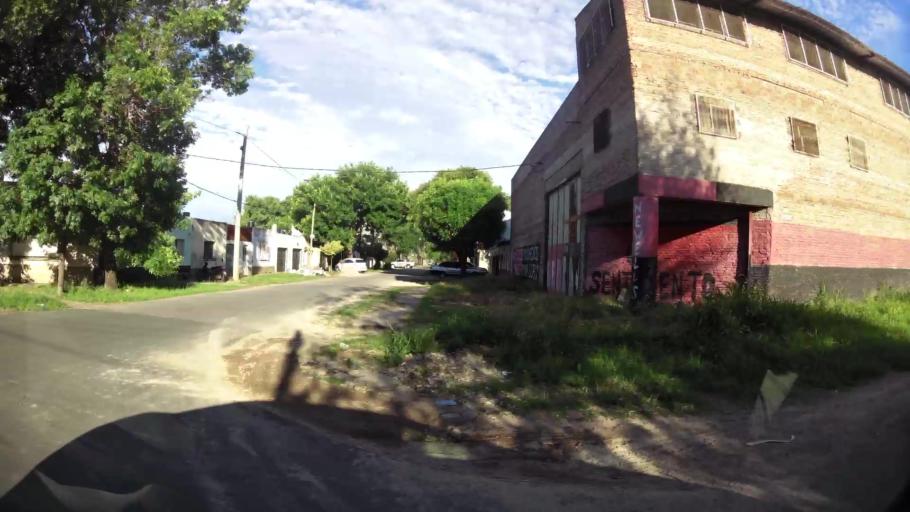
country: AR
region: Santa Fe
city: Gobernador Galvez
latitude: -32.9881
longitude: -60.6702
